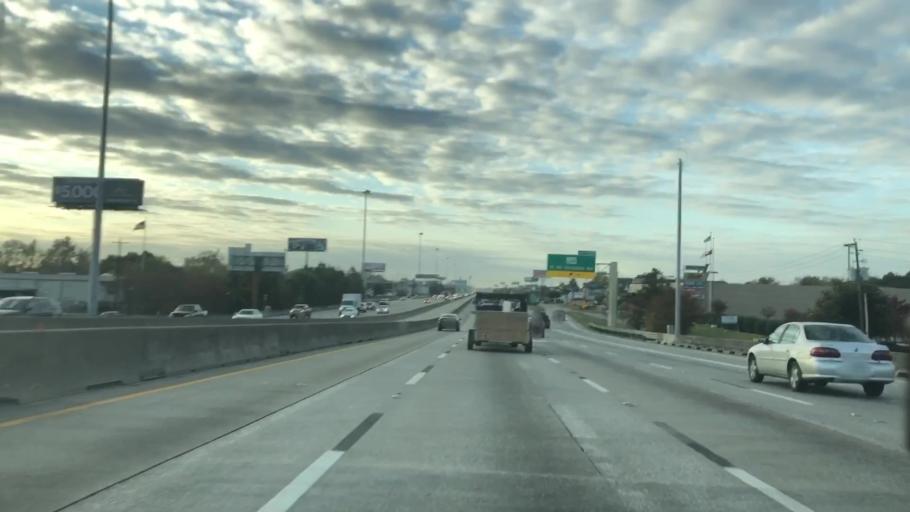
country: US
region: Texas
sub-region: Harris County
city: Aldine
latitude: 29.9137
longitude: -95.4127
